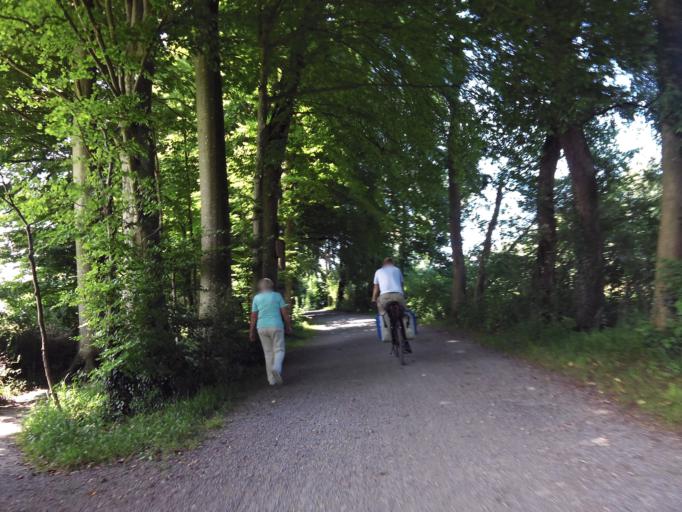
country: CH
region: Saint Gallen
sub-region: Wahlkreis Rheintal
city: Rheineck
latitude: 47.4844
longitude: 9.5778
